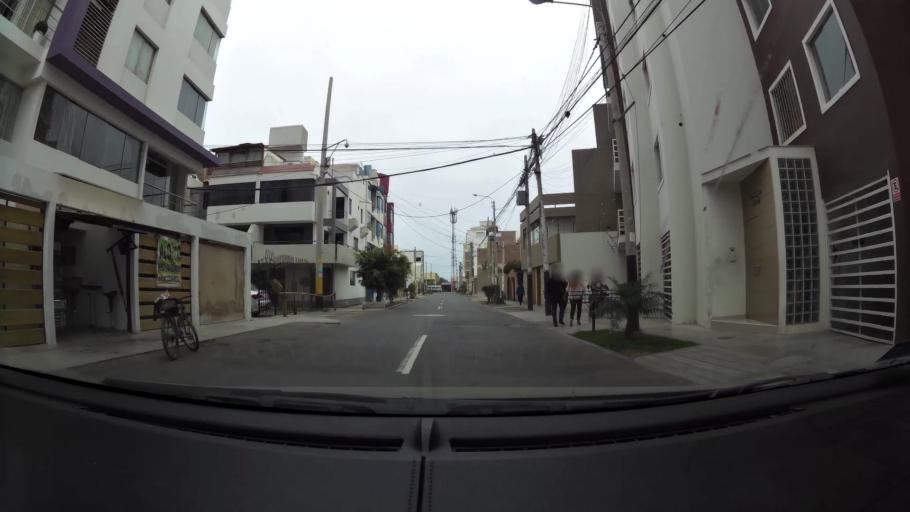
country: PE
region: La Libertad
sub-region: Provincia de Trujillo
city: Buenos Aires
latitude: -8.1346
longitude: -79.0409
